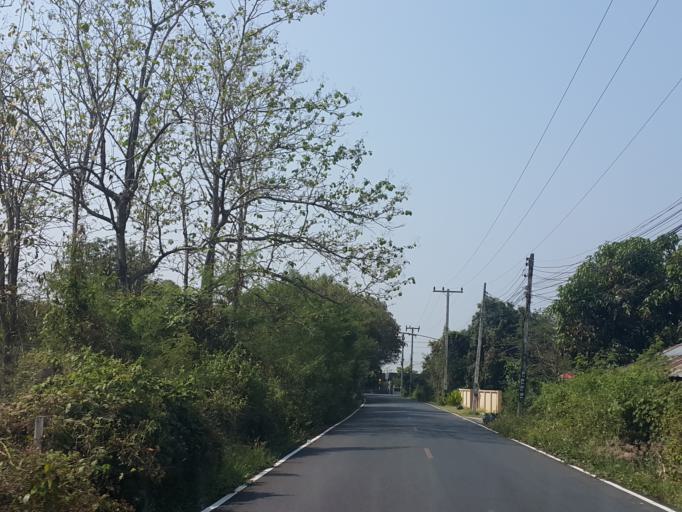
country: TH
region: Chiang Mai
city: San Kamphaeng
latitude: 18.7514
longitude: 99.1387
